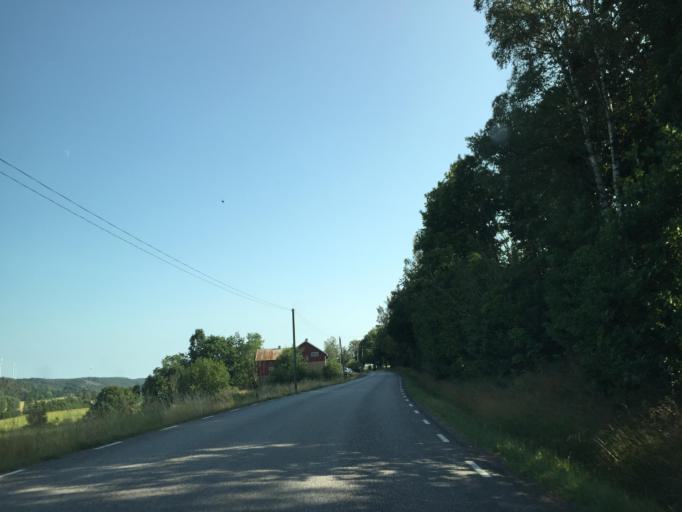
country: SE
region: Vaestra Goetaland
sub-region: Lilla Edets Kommun
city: Lilla Edet
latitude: 58.1848
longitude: 12.1175
